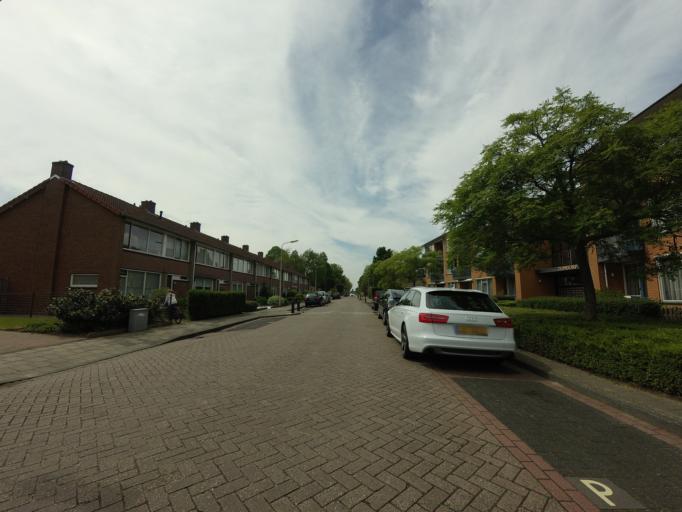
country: NL
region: North Brabant
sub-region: Gemeente Moerdijk
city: Willemstad
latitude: 51.7336
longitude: 4.4347
